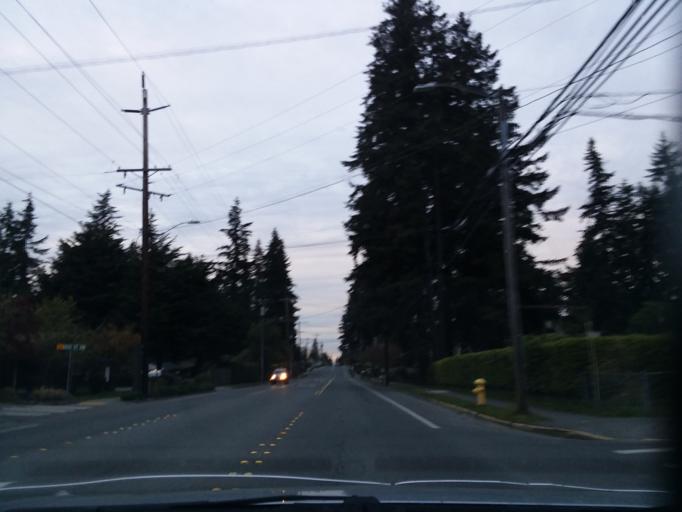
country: US
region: Washington
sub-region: Snohomish County
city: Lynnwood
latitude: 47.8160
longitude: -122.3358
